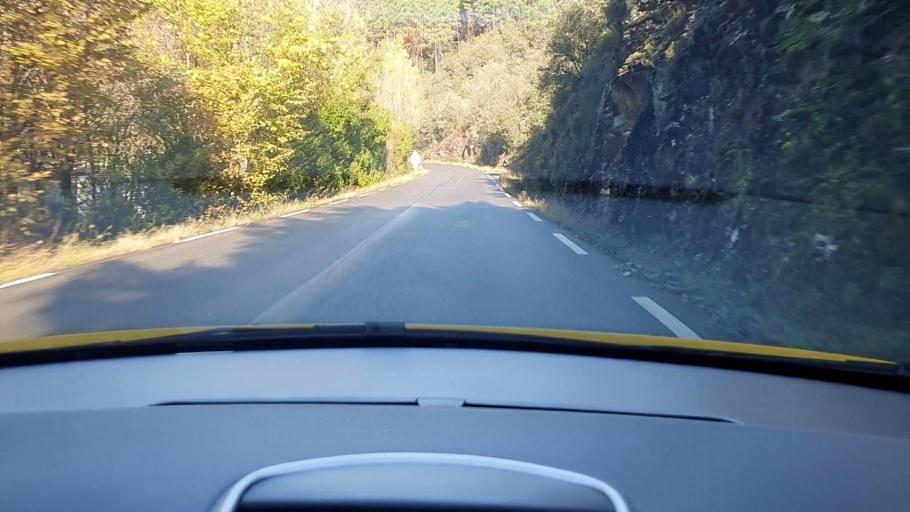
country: FR
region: Languedoc-Roussillon
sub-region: Departement du Gard
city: Valleraugue
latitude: 44.1360
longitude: 3.7577
